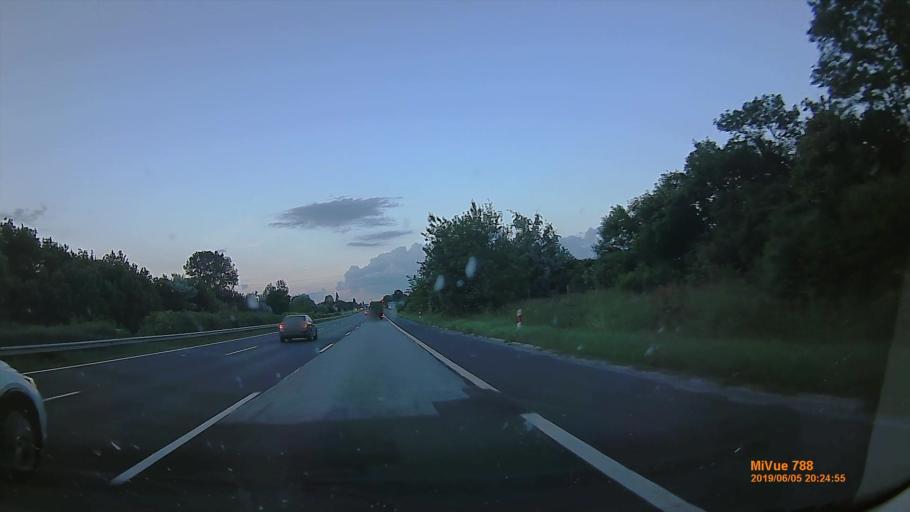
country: HU
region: Fejer
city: Martonvasar
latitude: 47.3355
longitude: 18.7825
